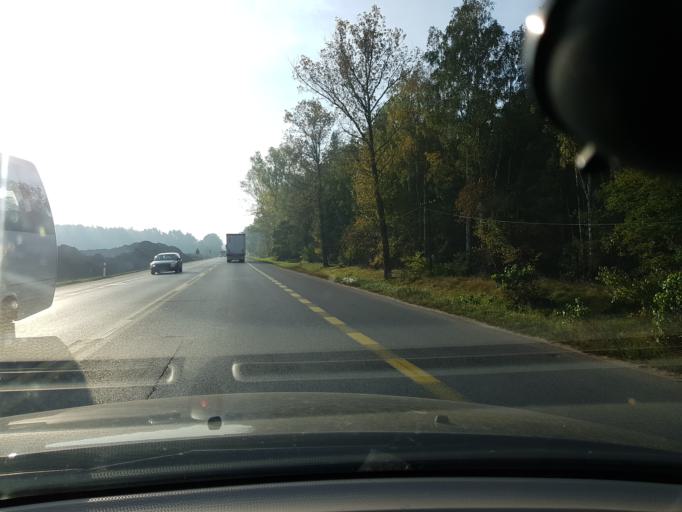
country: PL
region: Masovian Voivodeship
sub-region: Powiat otwocki
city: Otwock
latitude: 52.1502
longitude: 21.3177
